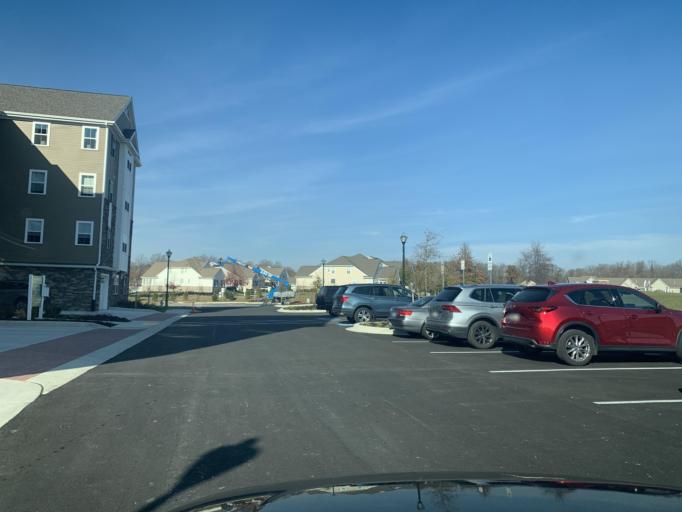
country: US
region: Maryland
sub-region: Harford County
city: Havre de Grace
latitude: 39.5435
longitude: -76.1213
